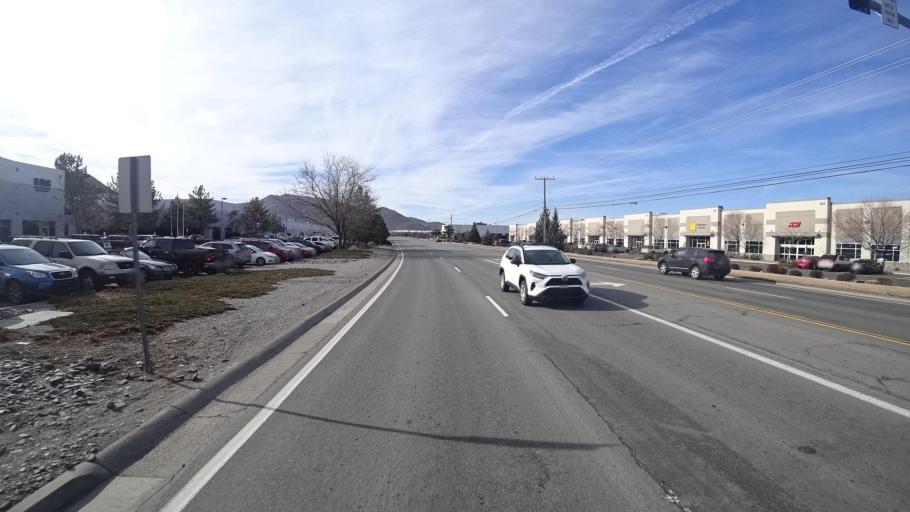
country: US
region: Nevada
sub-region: Washoe County
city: Sparks
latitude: 39.5369
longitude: -119.7041
